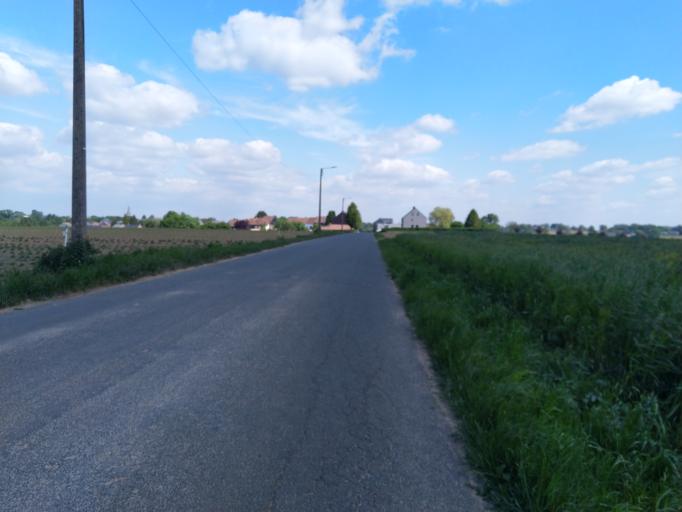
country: BE
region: Wallonia
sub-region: Province du Hainaut
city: Soignies
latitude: 50.5999
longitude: 4.0399
